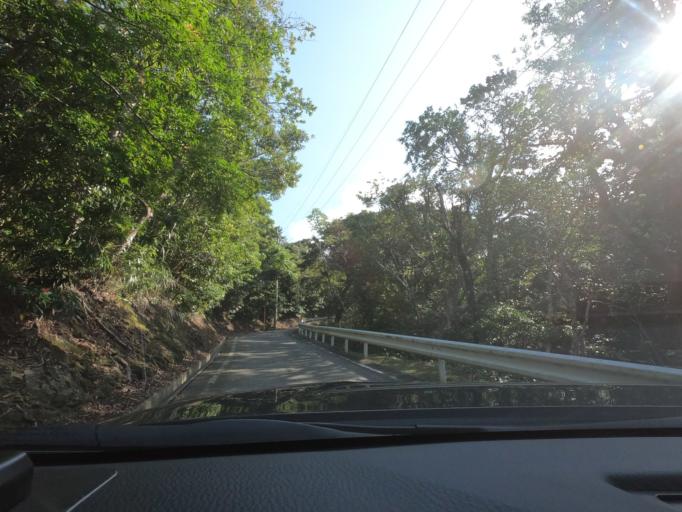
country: JP
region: Okinawa
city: Nago
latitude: 26.7561
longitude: 128.1991
